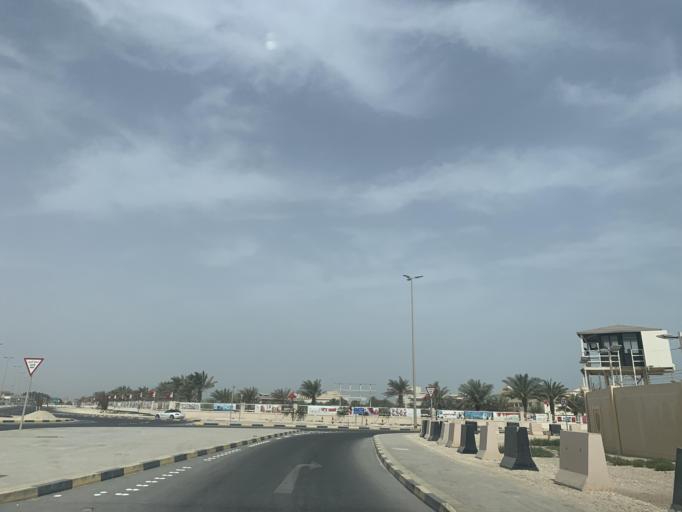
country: BH
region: Northern
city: Madinat `Isa
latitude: 26.1621
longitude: 50.5518
